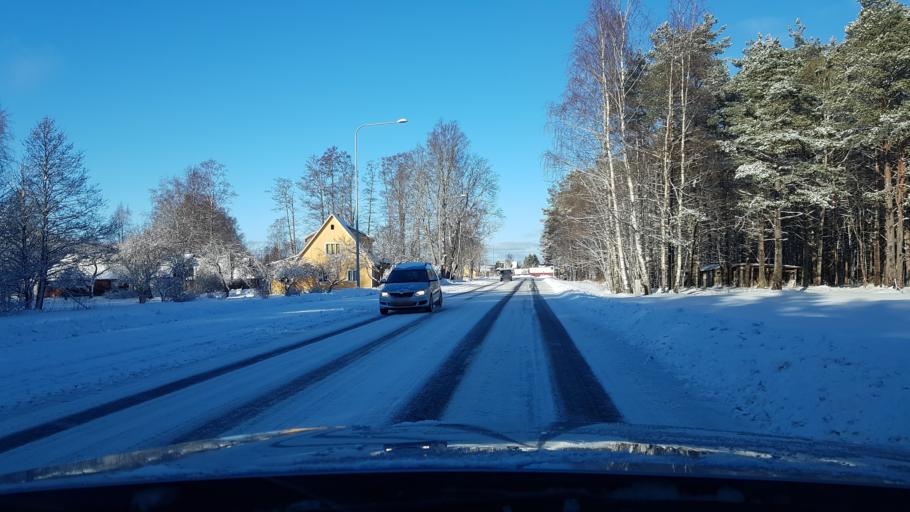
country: EE
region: Hiiumaa
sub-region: Kaerdla linn
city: Kardla
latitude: 58.9830
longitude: 22.7577
